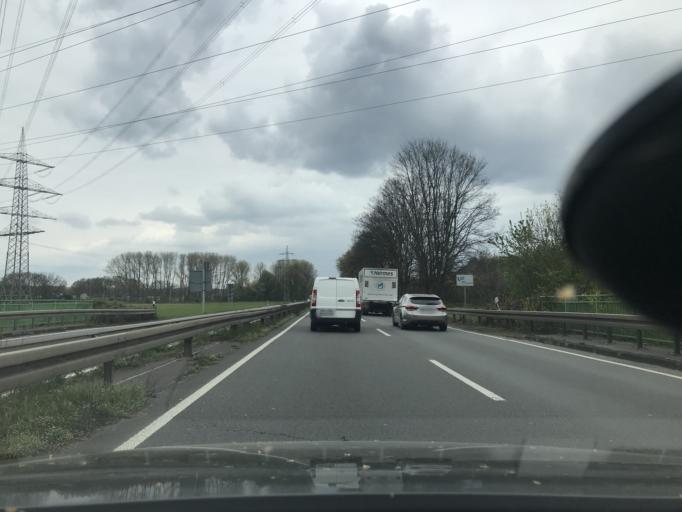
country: DE
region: North Rhine-Westphalia
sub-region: Regierungsbezirk Munster
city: Gladbeck
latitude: 51.5448
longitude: 6.9835
